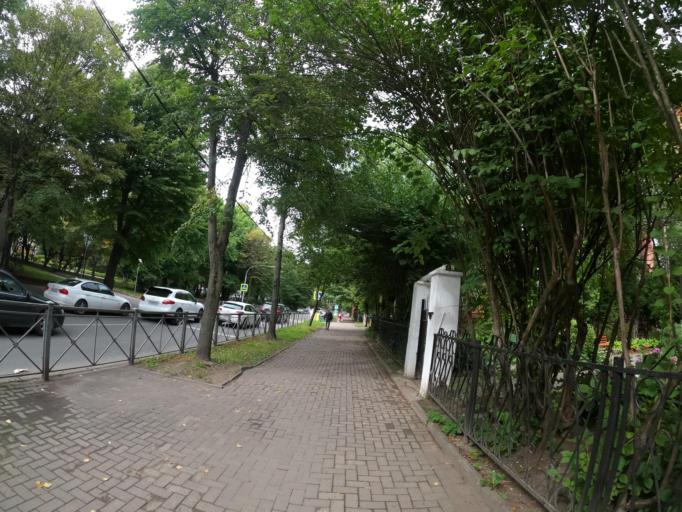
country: RU
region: Kaliningrad
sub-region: Gorod Kaliningrad
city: Kaliningrad
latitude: 54.7213
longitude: 20.4823
